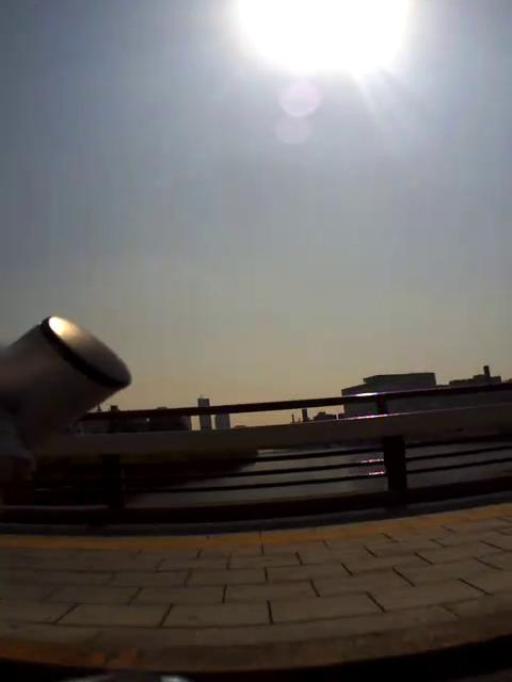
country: JP
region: Osaka
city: Osaka-shi
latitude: 34.6917
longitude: 135.5118
